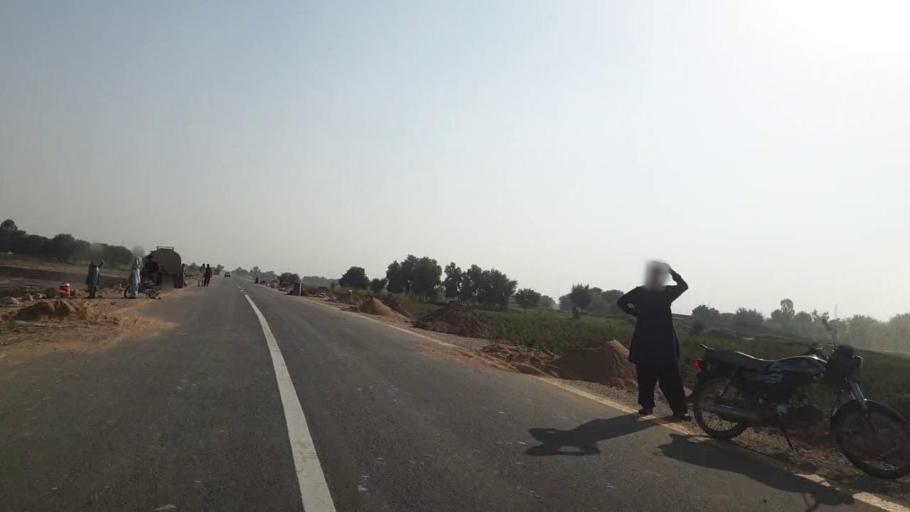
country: PK
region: Sindh
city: Bhan
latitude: 26.4947
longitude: 67.7801
